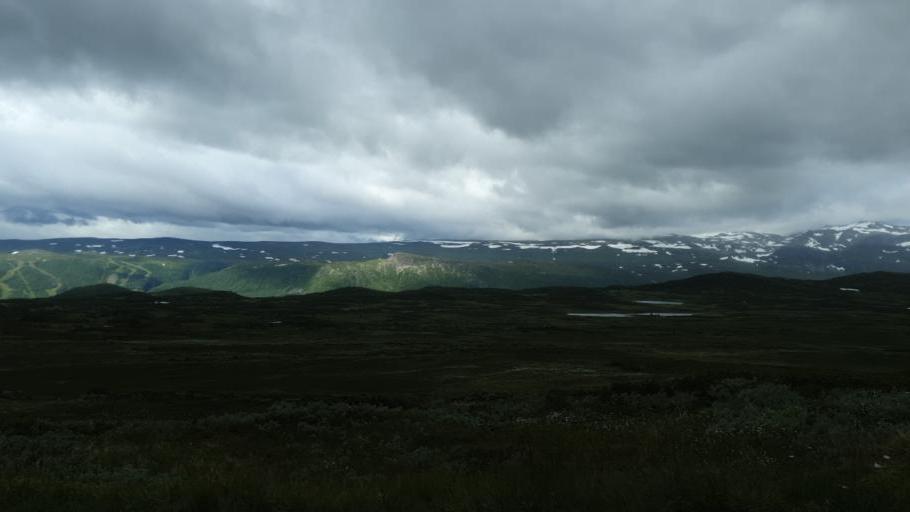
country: NO
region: Oppland
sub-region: Vestre Slidre
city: Slidre
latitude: 61.2769
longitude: 8.8535
